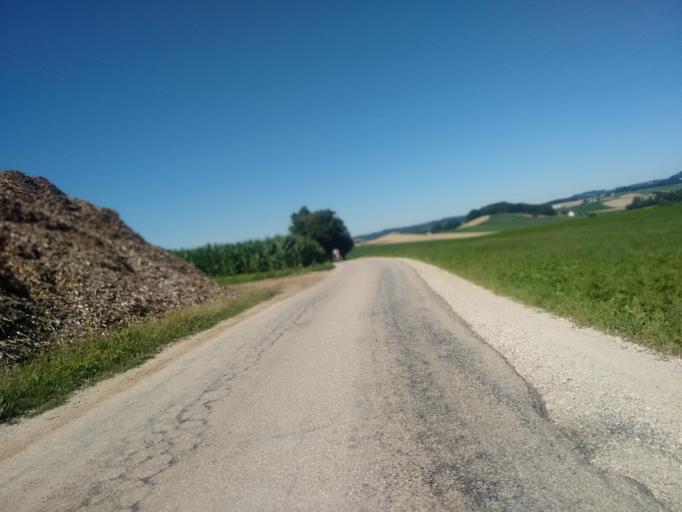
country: AT
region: Upper Austria
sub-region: Wels-Land
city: Buchkirchen
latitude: 48.2190
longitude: 14.0003
